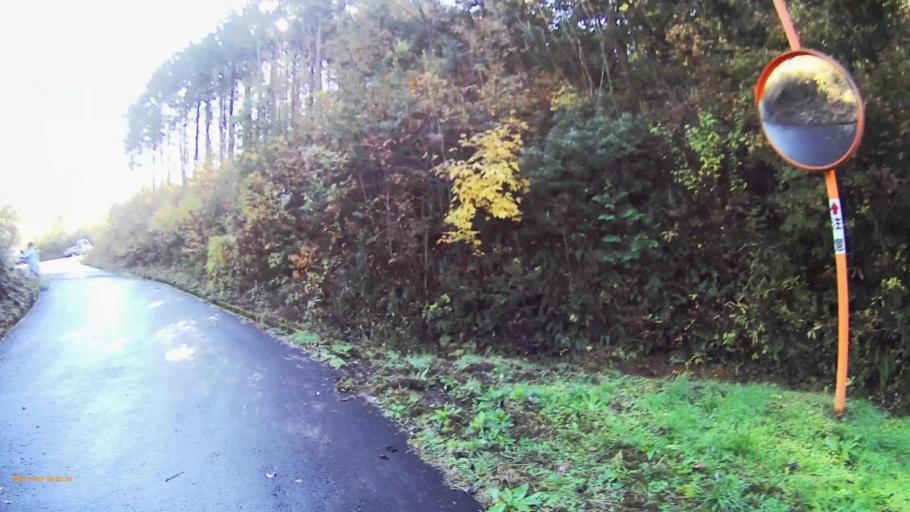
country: JP
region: Gifu
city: Mizunami
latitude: 35.4430
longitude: 137.3286
